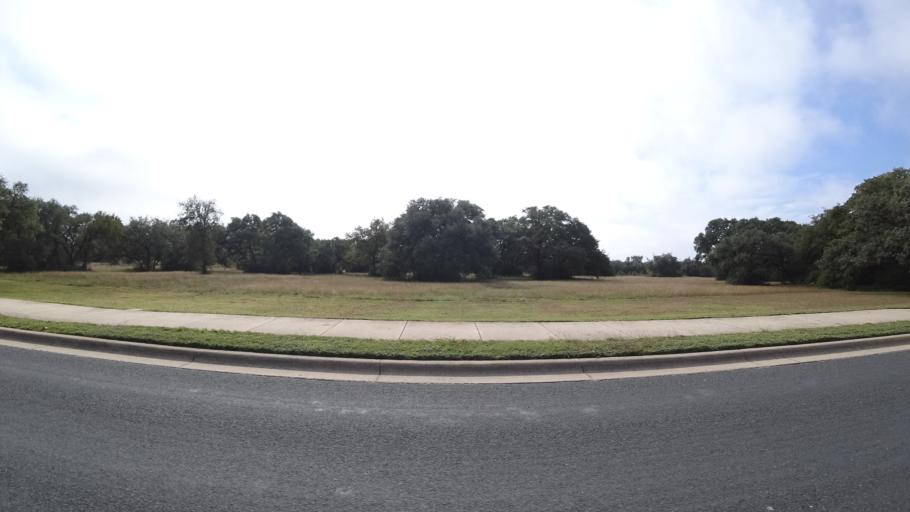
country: US
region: Texas
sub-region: Travis County
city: Shady Hollow
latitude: 30.2003
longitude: -97.8760
